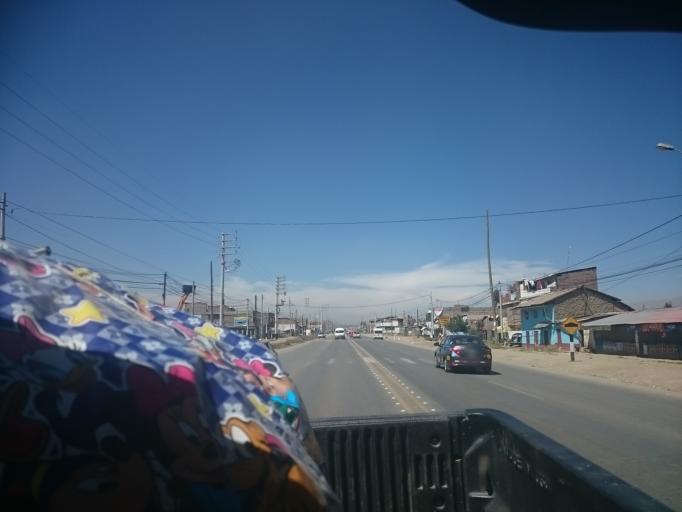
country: PE
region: Junin
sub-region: Provincia de Huancayo
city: San Agustin
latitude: -11.9984
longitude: -75.2534
